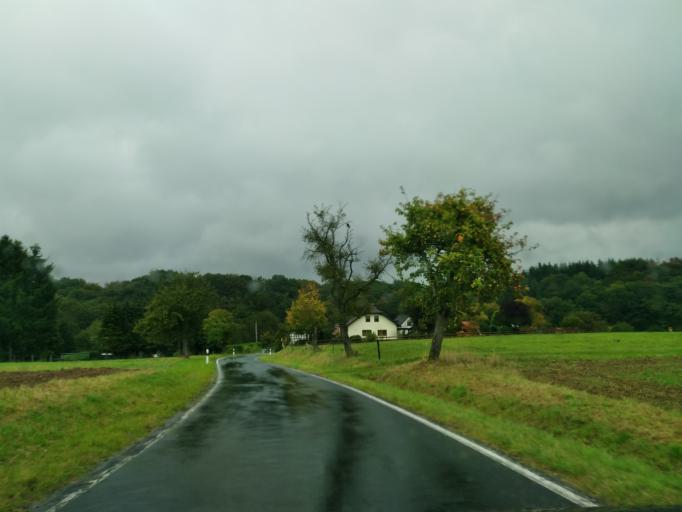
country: DE
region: Rheinland-Pfalz
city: Asbach
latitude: 50.6703
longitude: 7.4482
